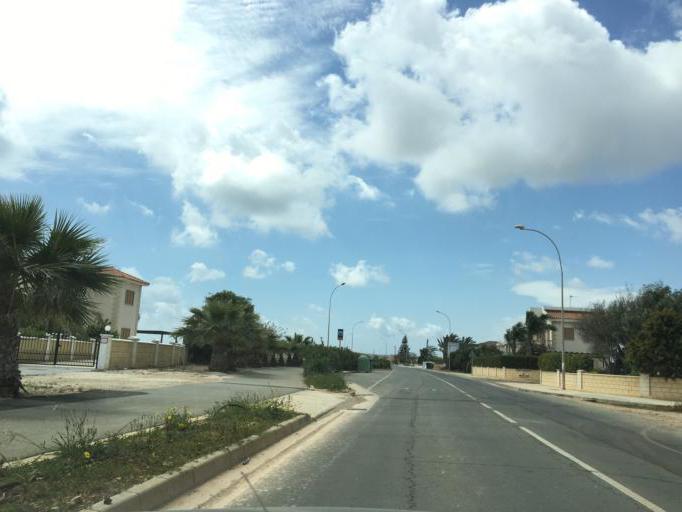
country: CY
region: Ammochostos
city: Liopetri
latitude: 34.9792
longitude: 33.9215
